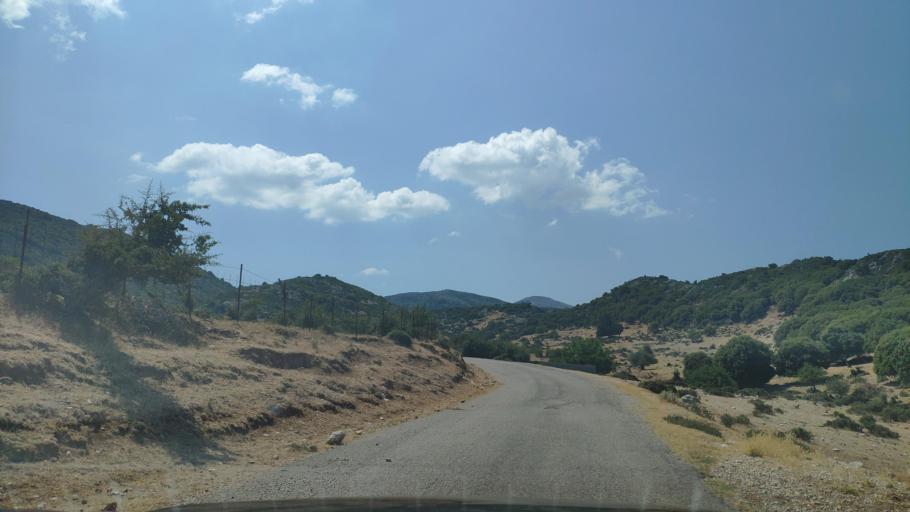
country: GR
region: West Greece
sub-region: Nomos Aitolias kai Akarnanias
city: Monastirakion
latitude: 38.8086
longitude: 20.9417
